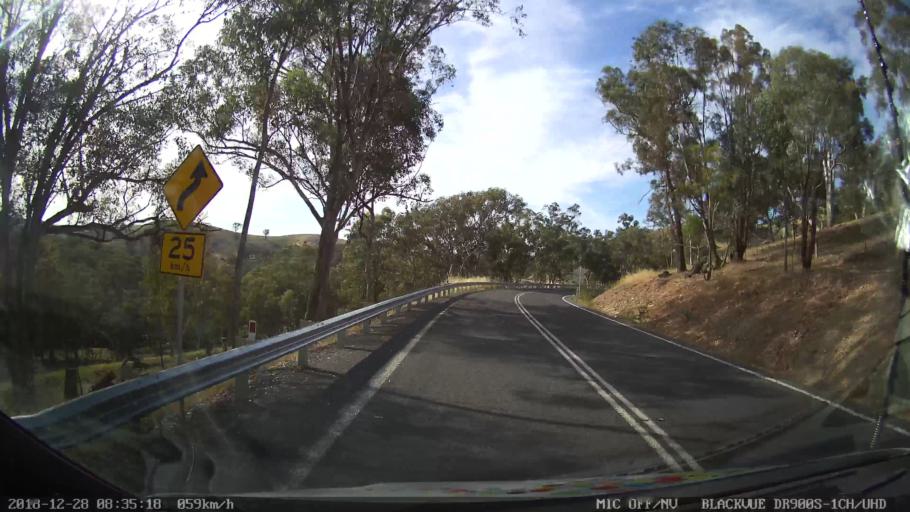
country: AU
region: New South Wales
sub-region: Blayney
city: Blayney
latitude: -33.9823
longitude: 149.3098
